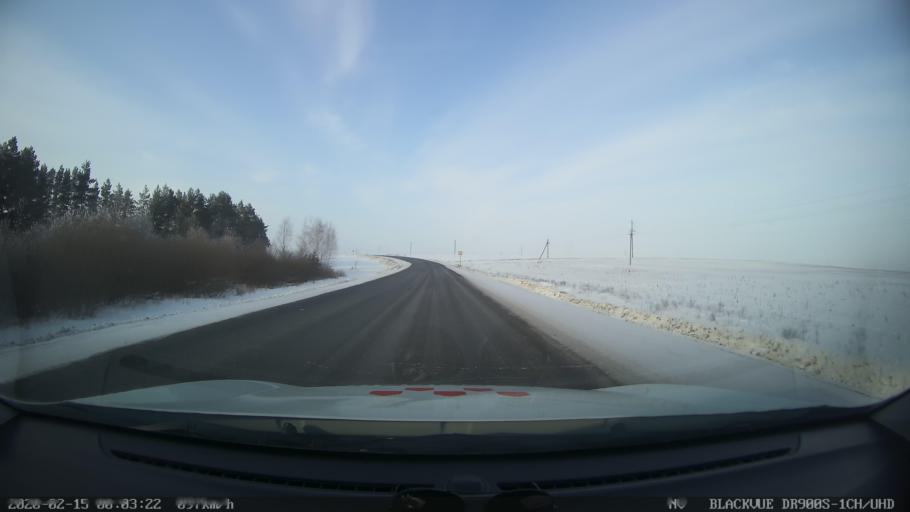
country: RU
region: Tatarstan
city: Kuybyshevskiy Zaton
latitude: 55.3709
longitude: 48.9982
